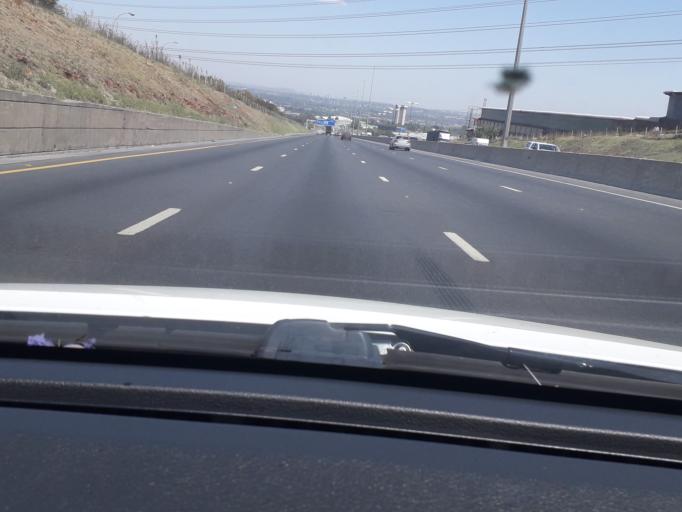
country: ZA
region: Gauteng
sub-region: Ekurhuleni Metropolitan Municipality
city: Germiston
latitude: -26.1650
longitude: 28.1802
